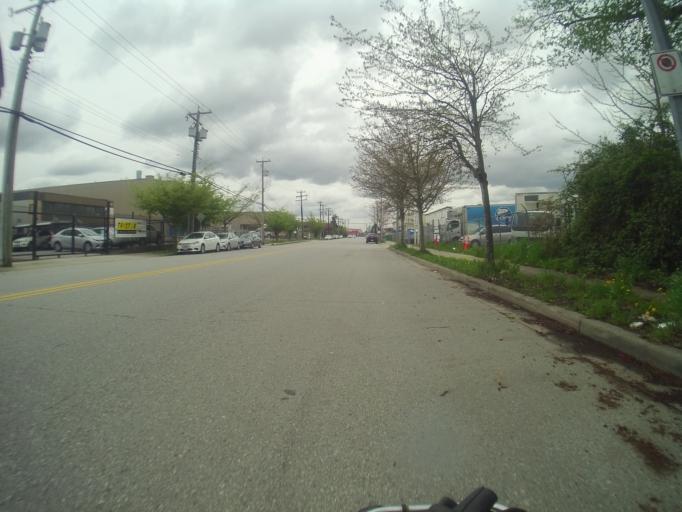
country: CA
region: British Columbia
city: Richmond
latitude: 49.1939
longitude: -123.0865
